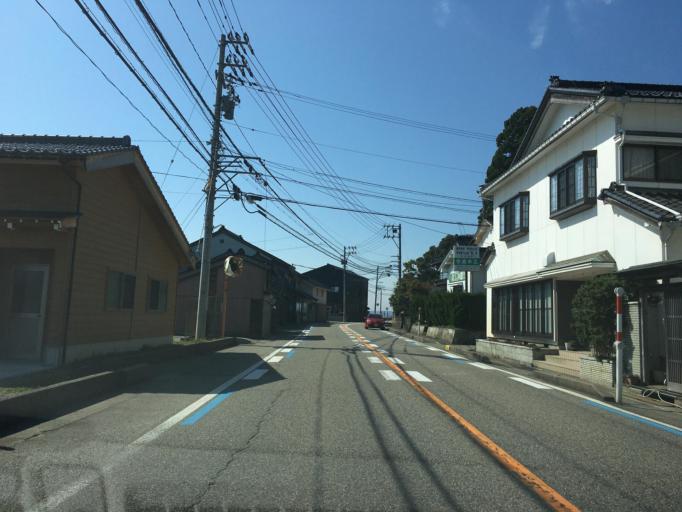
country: JP
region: Toyama
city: Himi
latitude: 36.8953
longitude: 137.0065
